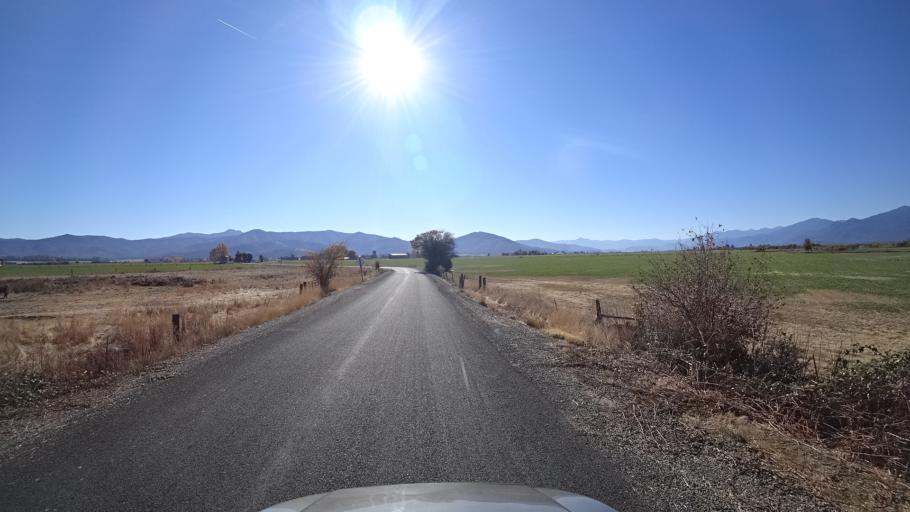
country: US
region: California
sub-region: Siskiyou County
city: Yreka
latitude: 41.5766
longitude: -122.8597
